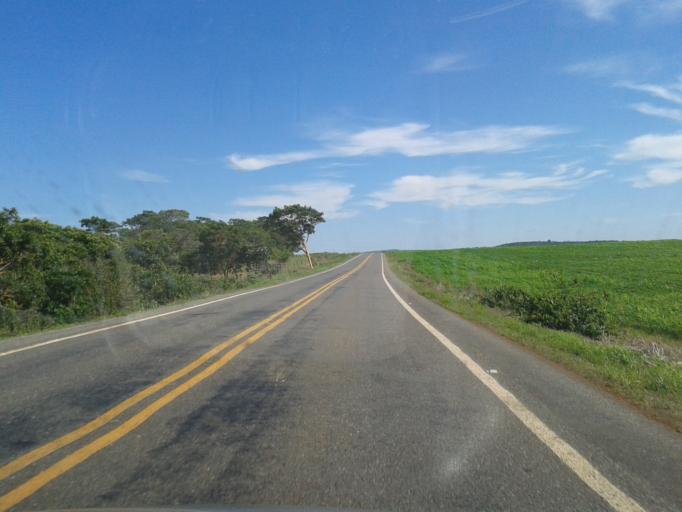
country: BR
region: Goias
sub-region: Piracanjuba
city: Piracanjuba
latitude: -17.3242
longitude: -48.8009
